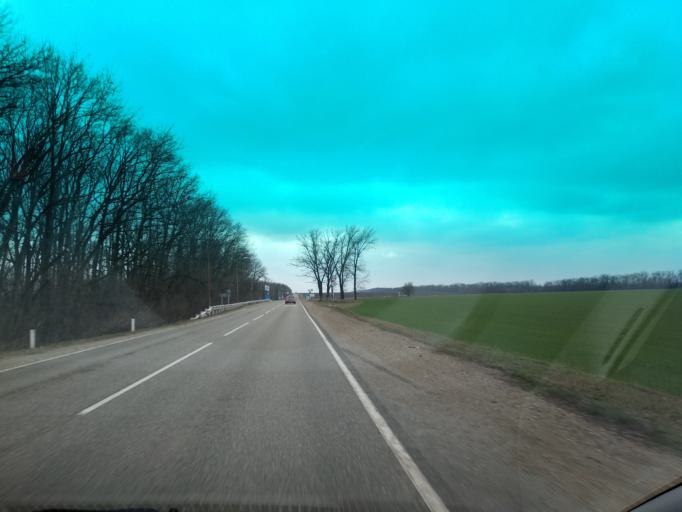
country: RU
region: Krasnodarskiy
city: Novorozhdestvenskaya
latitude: 45.7572
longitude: 39.9255
